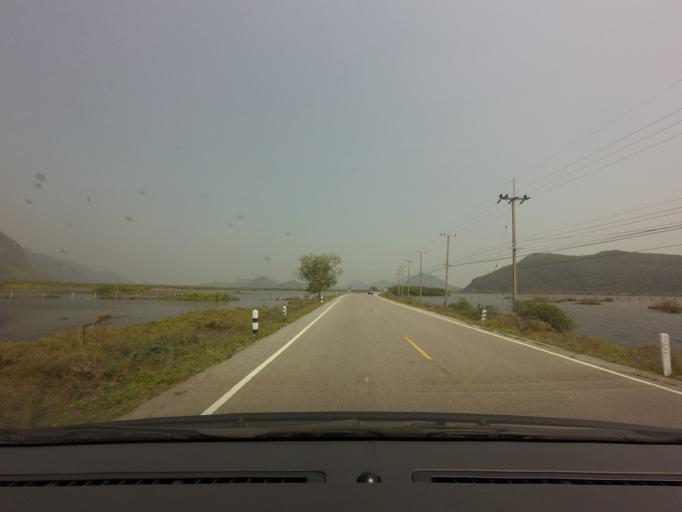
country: TH
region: Prachuap Khiri Khan
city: Kui Buri
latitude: 12.1560
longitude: 99.9770
